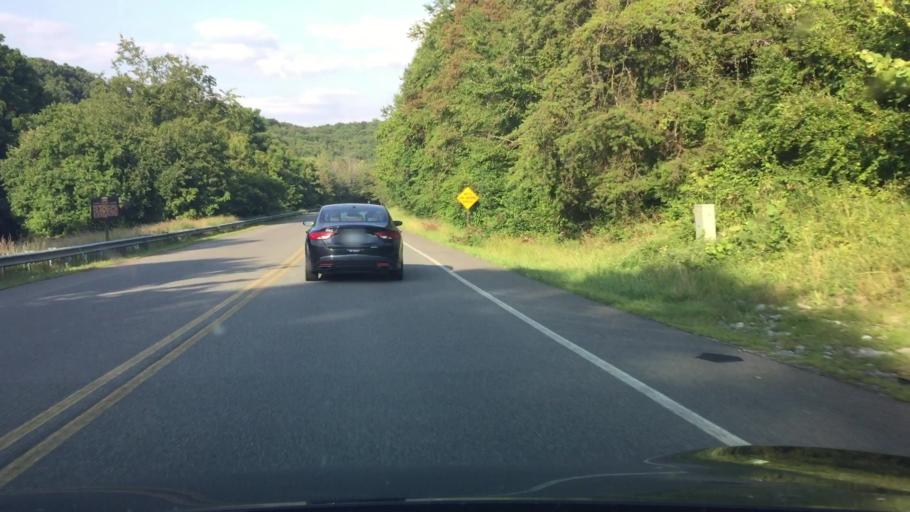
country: US
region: Virginia
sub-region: City of Radford
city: Radford
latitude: 37.1181
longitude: -80.5536
